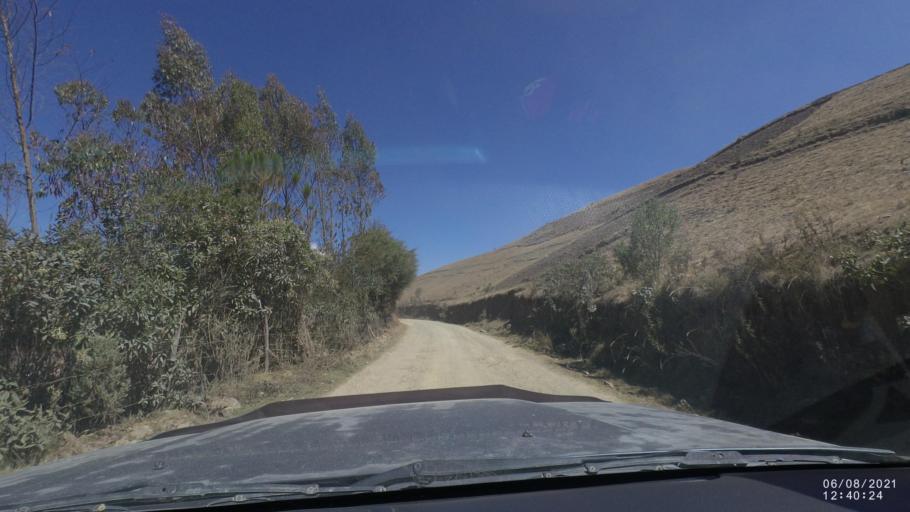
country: BO
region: Cochabamba
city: Colchani
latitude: -16.7836
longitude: -66.6642
